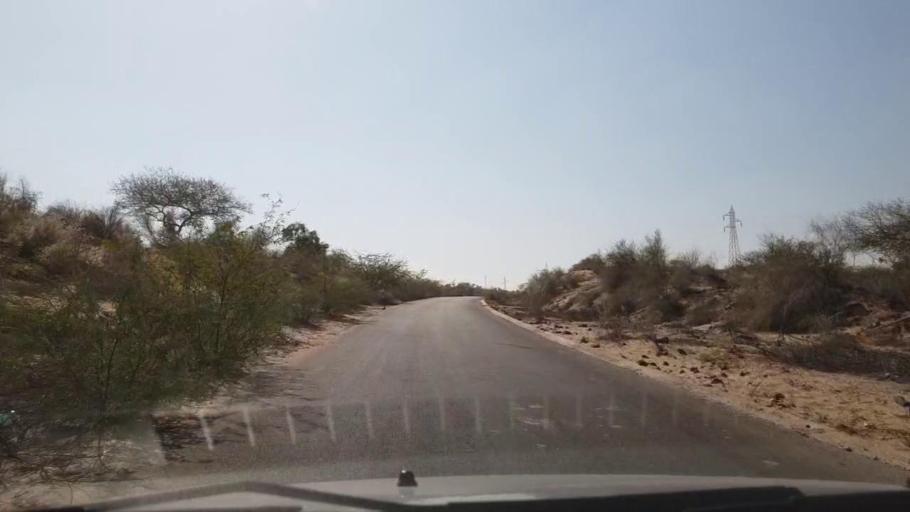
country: PK
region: Sindh
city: Mithi
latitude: 24.6345
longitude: 69.7419
